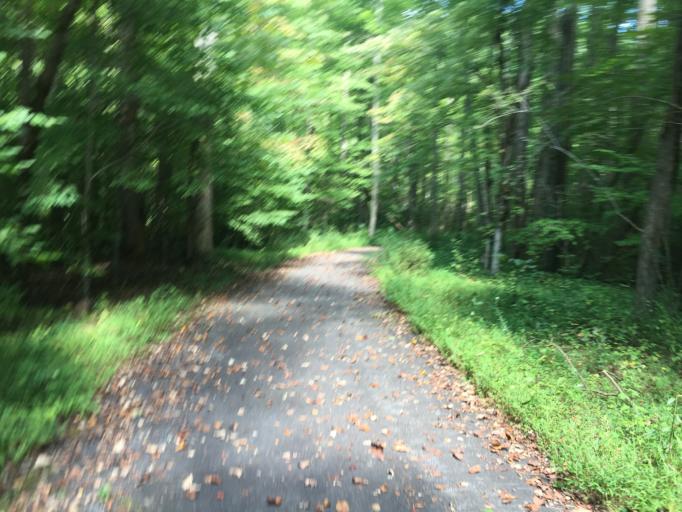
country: US
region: North Carolina
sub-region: Graham County
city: Robbinsville
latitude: 35.2750
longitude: -83.6801
